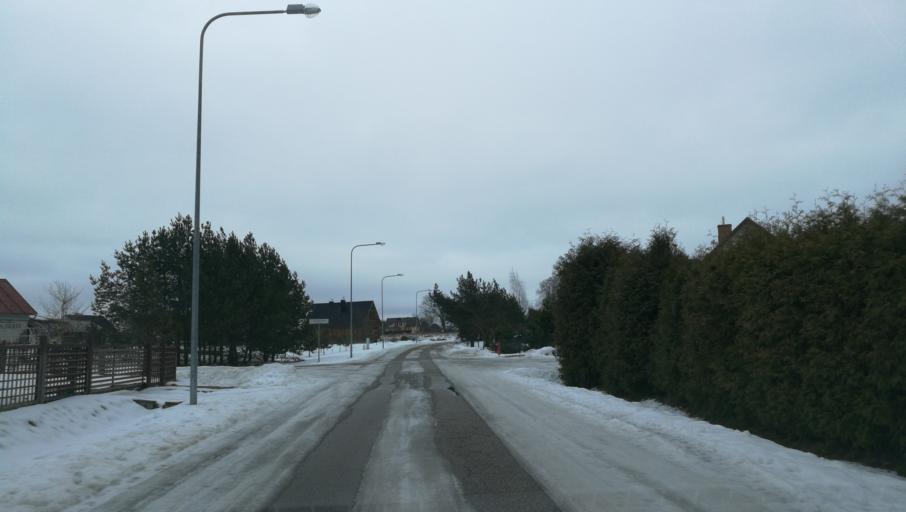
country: LT
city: Trakai
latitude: 54.6167
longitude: 24.9169
